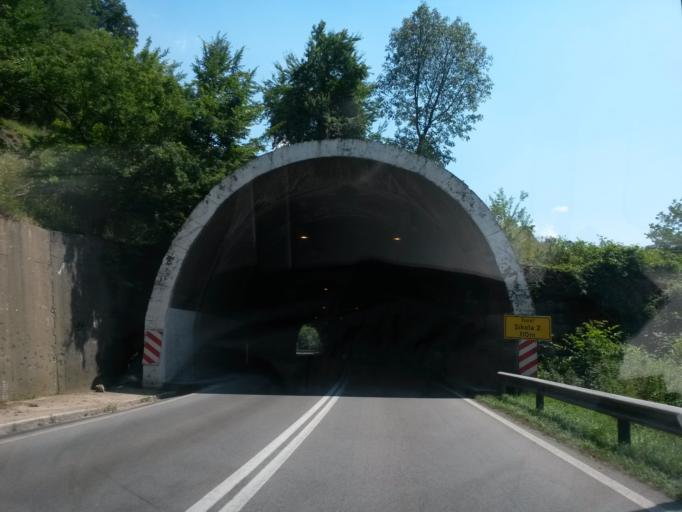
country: BA
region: Federation of Bosnia and Herzegovina
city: Maglaj
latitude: 44.5309
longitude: 18.0869
